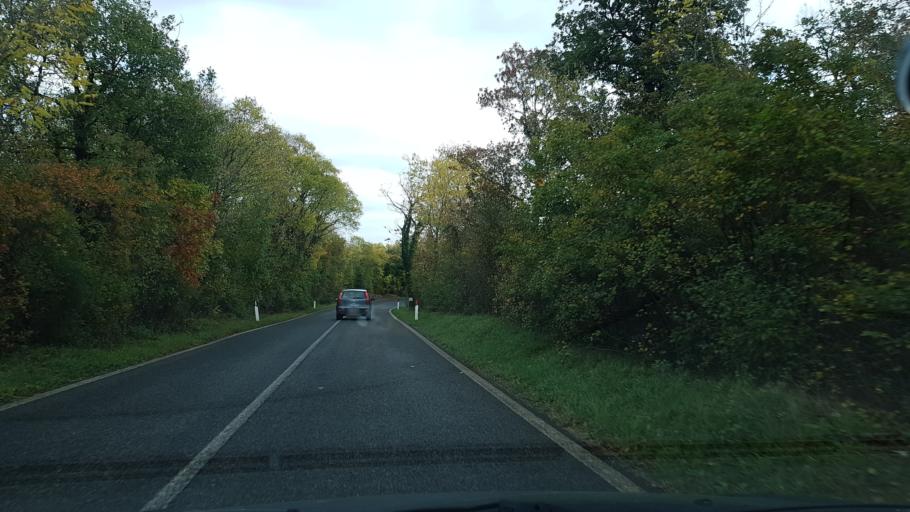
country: IT
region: Friuli Venezia Giulia
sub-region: Provincia di Gorizia
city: Doberdo del Lago
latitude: 45.8534
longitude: 13.5432
